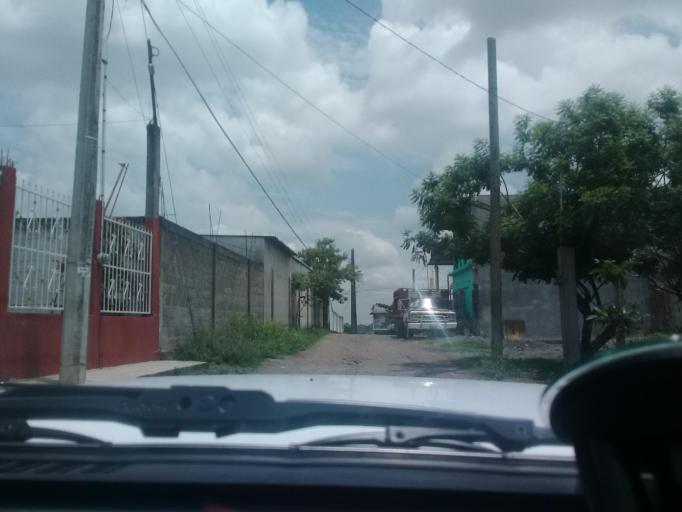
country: MX
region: Veracruz
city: Paso de Ovejas
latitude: 19.2927
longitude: -96.4428
